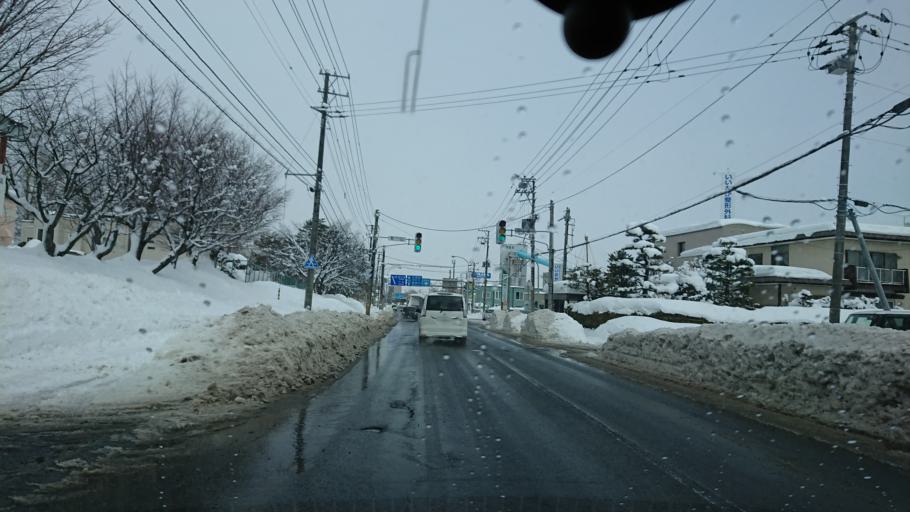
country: JP
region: Hokkaido
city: Sapporo
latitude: 42.9707
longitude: 141.3436
